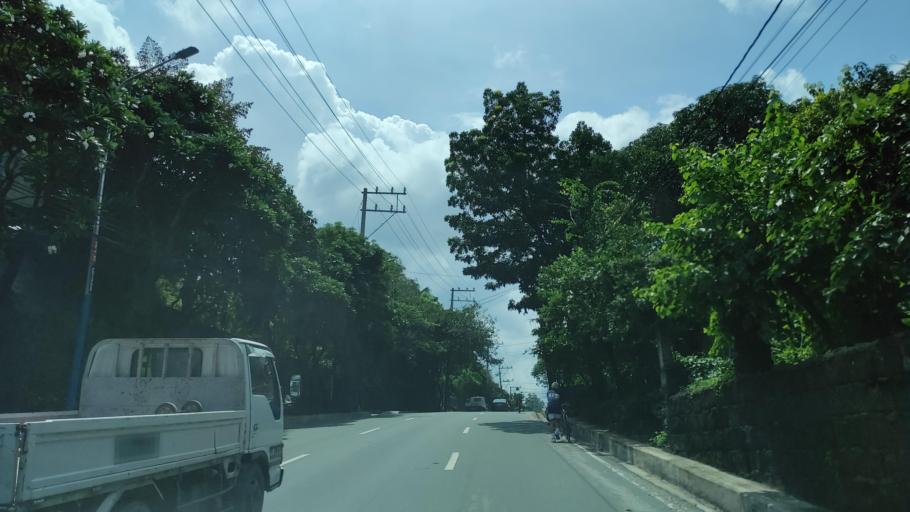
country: PH
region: Calabarzon
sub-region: Province of Rizal
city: Cainta
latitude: 14.5868
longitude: 121.1583
